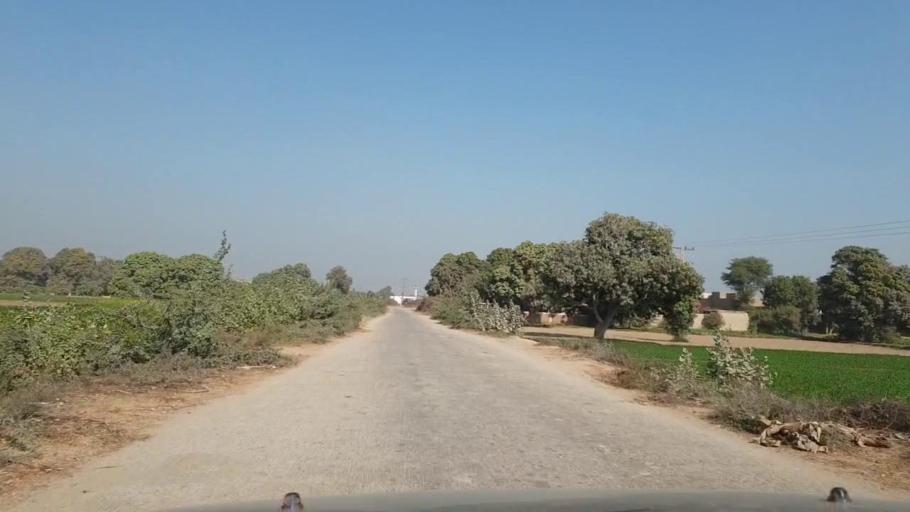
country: PK
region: Sindh
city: Matiari
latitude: 25.5967
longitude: 68.6010
